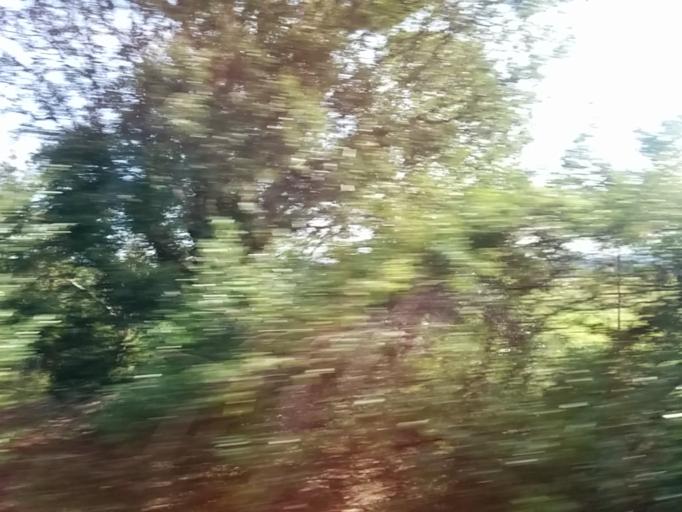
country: JP
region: Nara
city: Nara-shi
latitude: 34.6902
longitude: 135.7899
